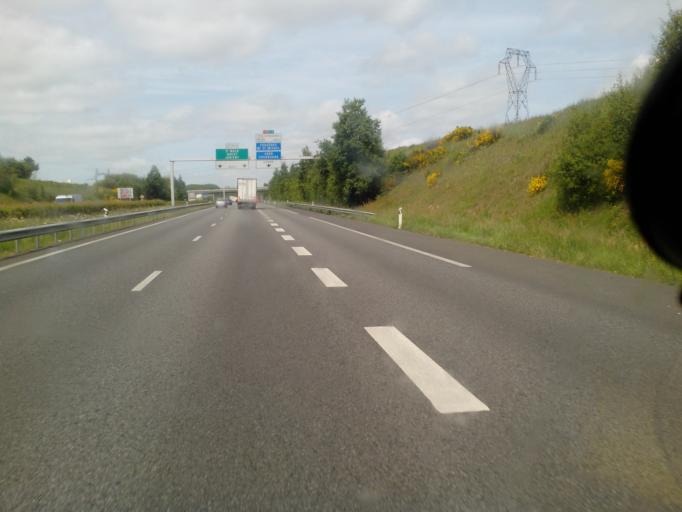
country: FR
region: Brittany
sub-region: Departement d'Ille-et-Vilaine
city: Fouillard
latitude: 48.1443
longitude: -1.5886
